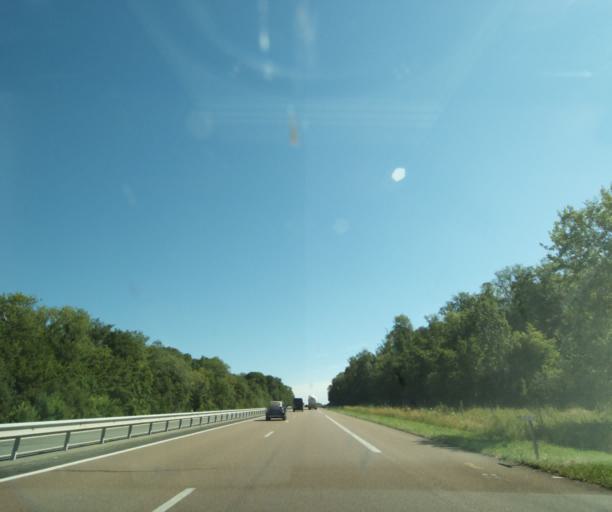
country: FR
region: Champagne-Ardenne
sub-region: Departement de la Haute-Marne
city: Saulxures
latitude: 48.0615
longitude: 5.5859
